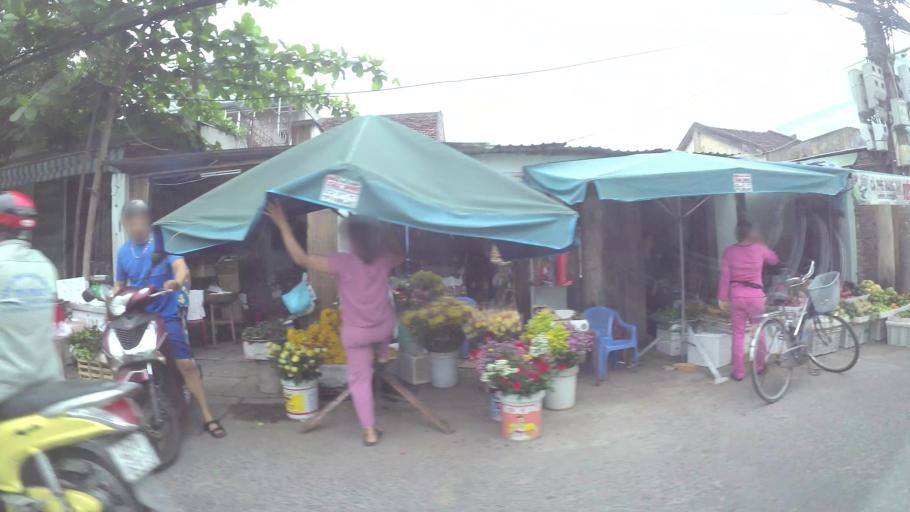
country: VN
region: Da Nang
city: Thanh Khe
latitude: 16.0539
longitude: 108.1838
